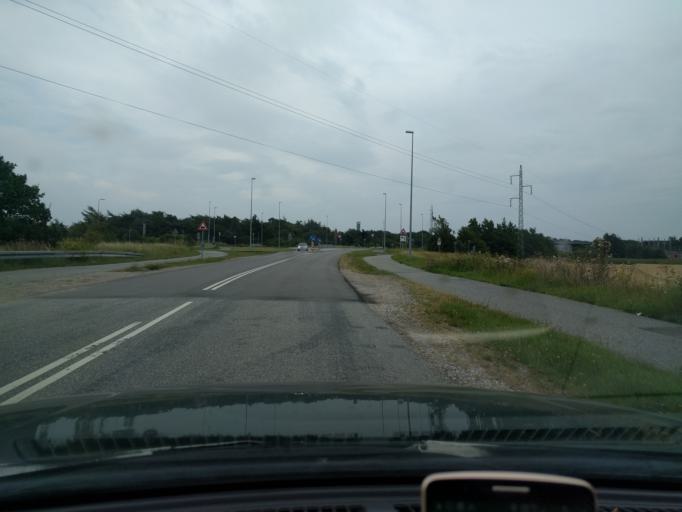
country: DK
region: Zealand
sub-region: Slagelse Kommune
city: Korsor
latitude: 55.3538
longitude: 11.1427
